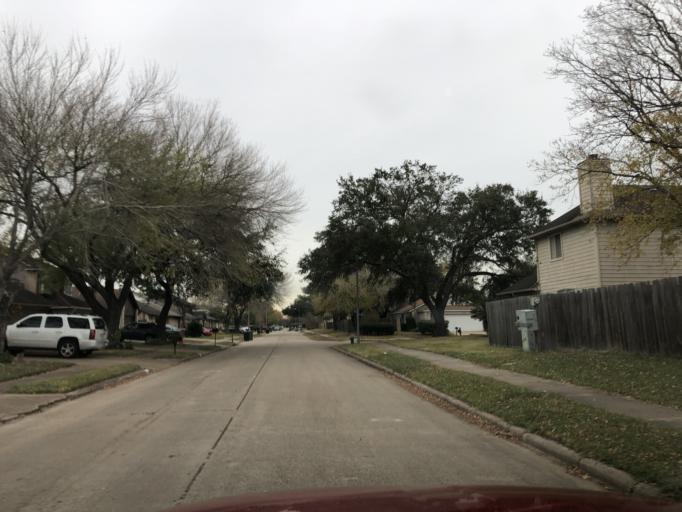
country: US
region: Texas
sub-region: Fort Bend County
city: Missouri City
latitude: 29.6400
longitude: -95.5311
